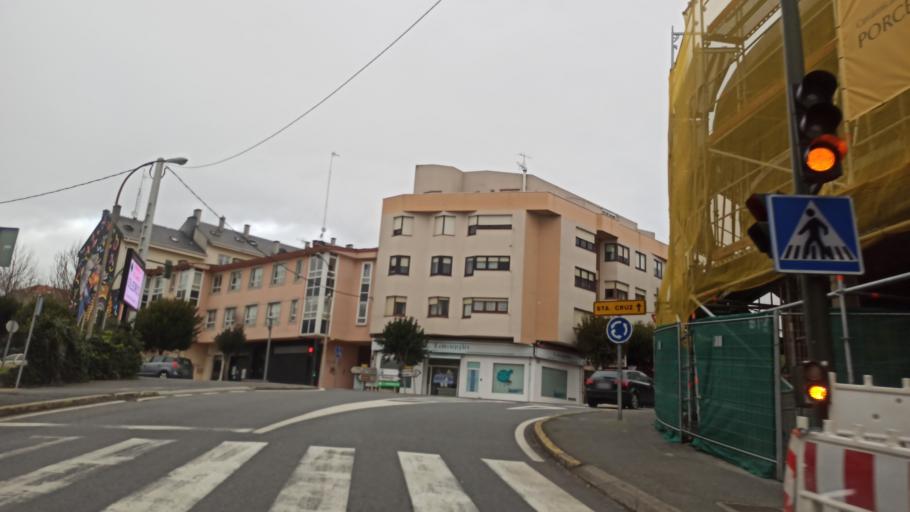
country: ES
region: Galicia
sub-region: Provincia da Coruna
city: Cambre
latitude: 43.3323
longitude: -8.3712
